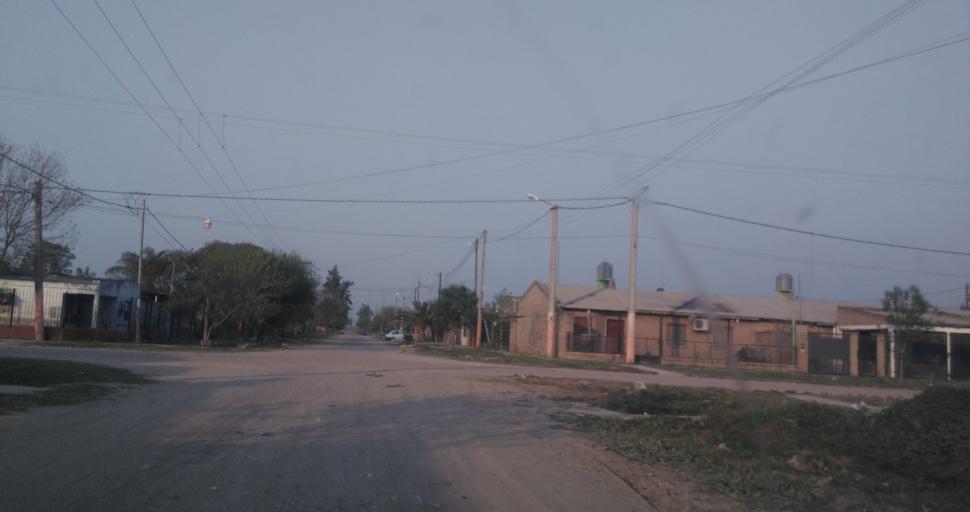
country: AR
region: Chaco
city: Resistencia
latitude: -27.4772
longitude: -59.0051
